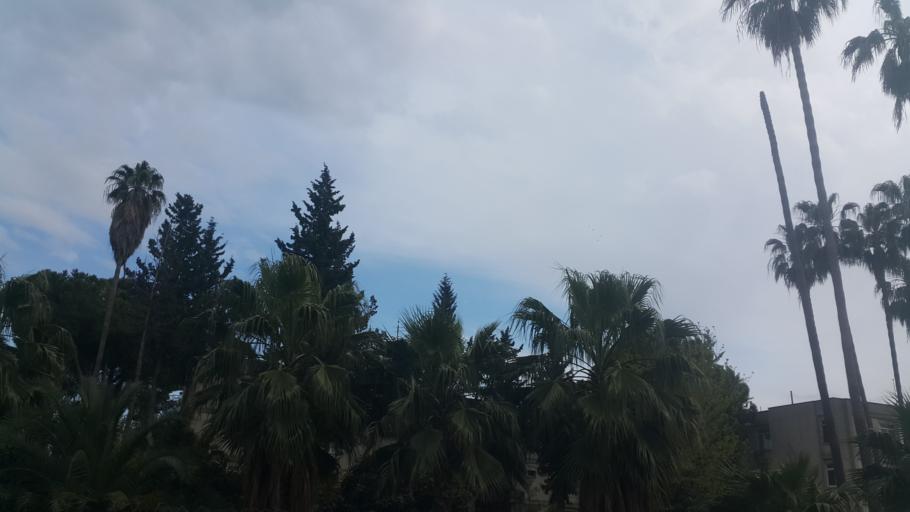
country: TR
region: Adana
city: Seyhan
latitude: 36.9930
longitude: 35.1921
